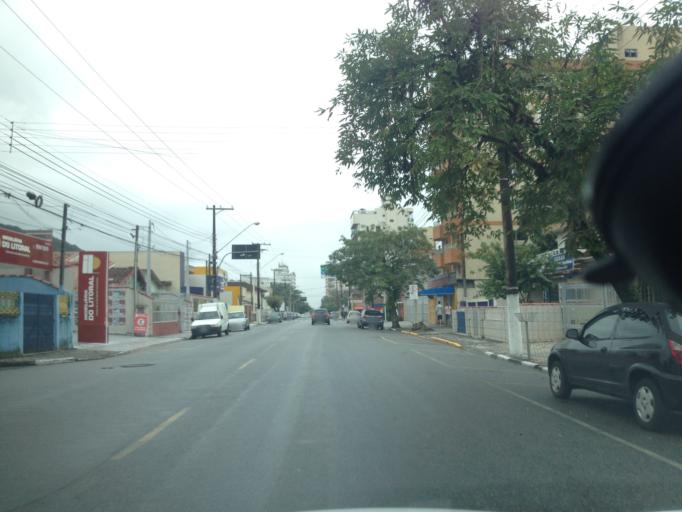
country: BR
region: Sao Paulo
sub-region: Mongagua
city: Mongagua
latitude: -24.0966
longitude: -46.6239
